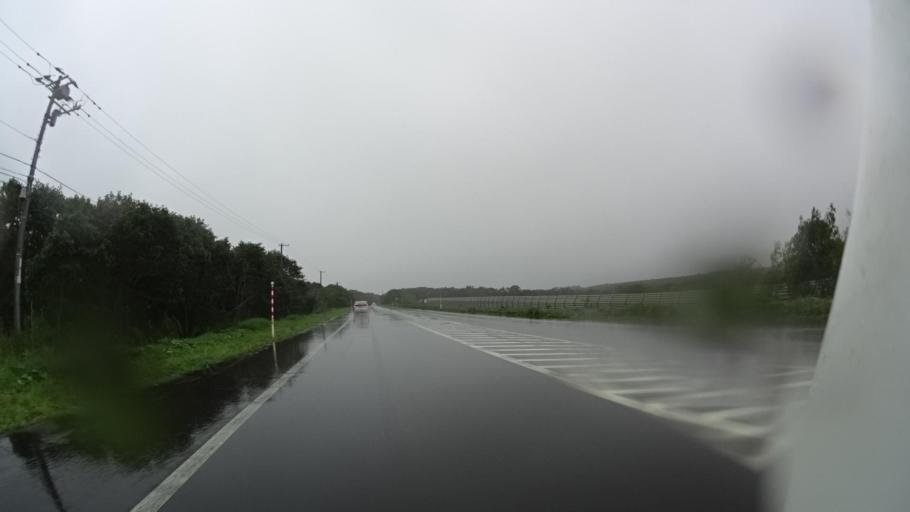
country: JP
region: Hokkaido
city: Nemuro
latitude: 43.2377
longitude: 145.2736
